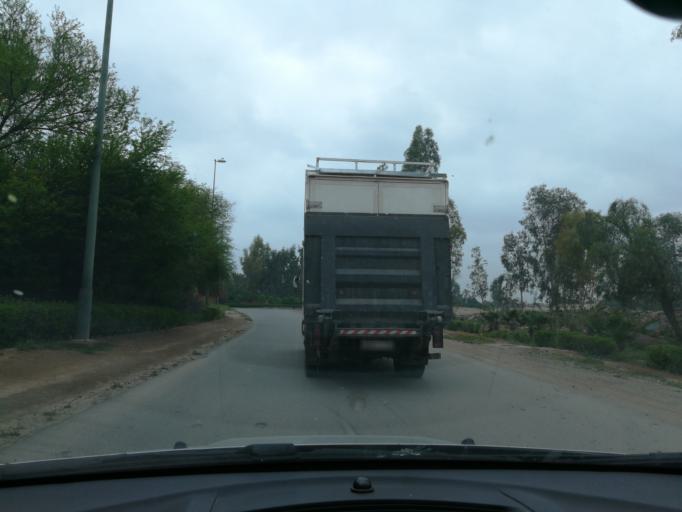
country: MA
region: Marrakech-Tensift-Al Haouz
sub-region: Marrakech
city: Marrakesh
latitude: 31.6576
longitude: -7.9834
